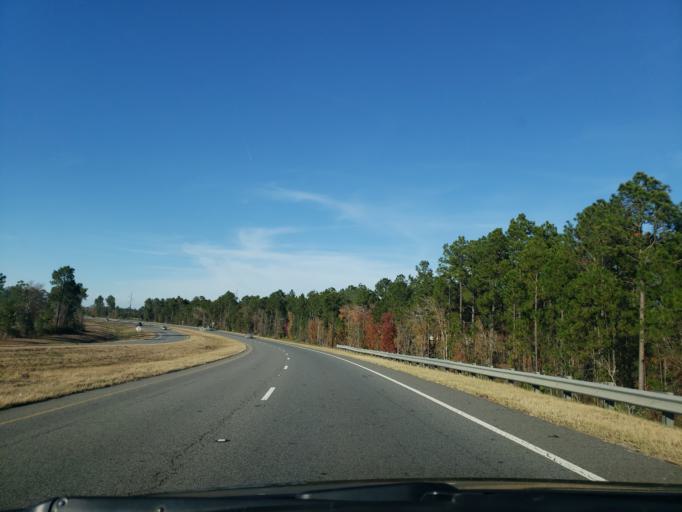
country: US
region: Georgia
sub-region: Ware County
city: Deenwood
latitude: 31.2364
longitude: -82.4267
